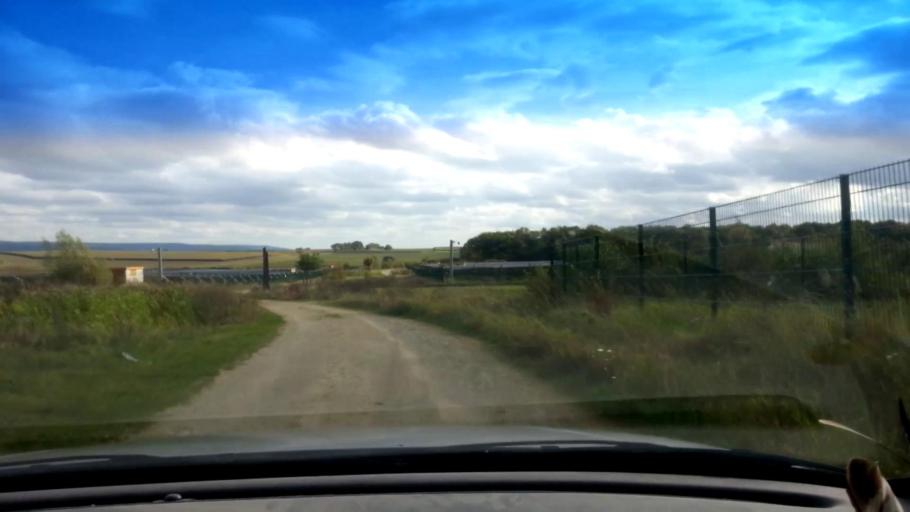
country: DE
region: Bavaria
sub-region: Upper Franconia
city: Zapfendorf
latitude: 49.9822
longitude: 10.9630
